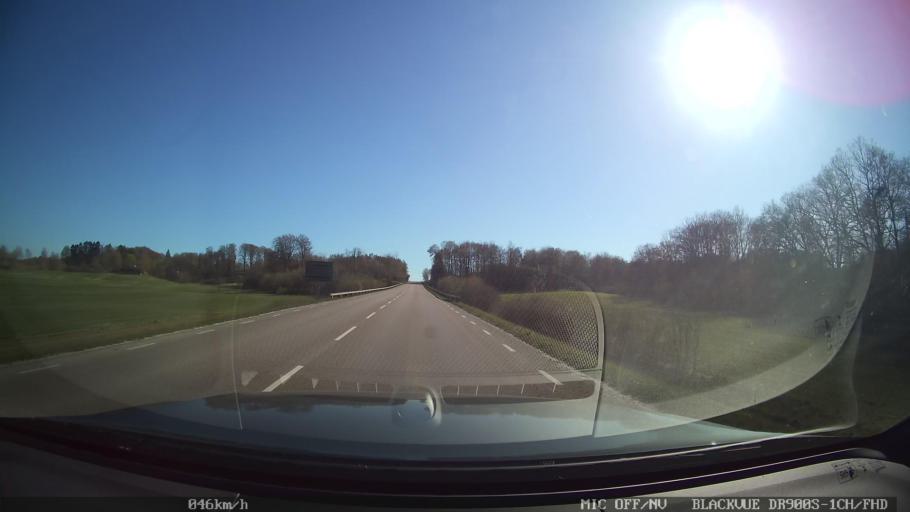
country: SE
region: Skane
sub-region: Klippans Kommun
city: Ljungbyhed
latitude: 55.9953
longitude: 13.2829
